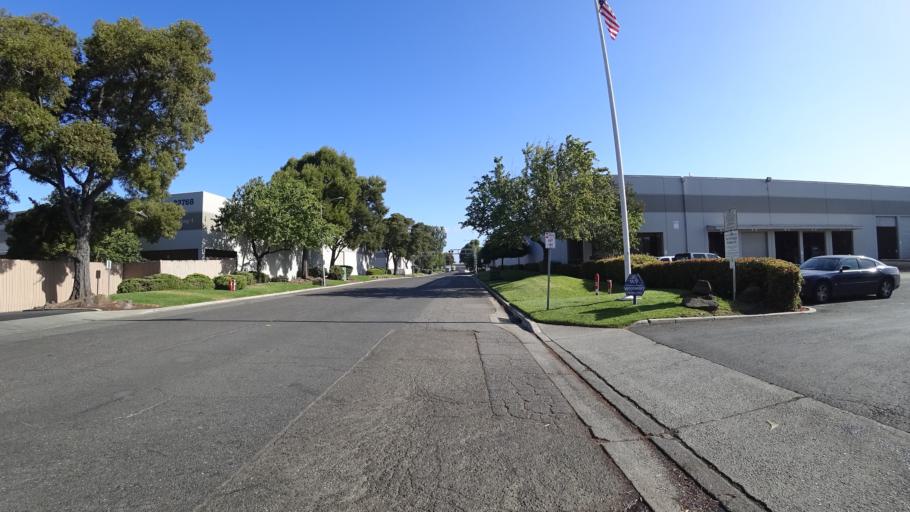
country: US
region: California
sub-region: Alameda County
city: San Lorenzo
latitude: 37.6394
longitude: -122.1266
